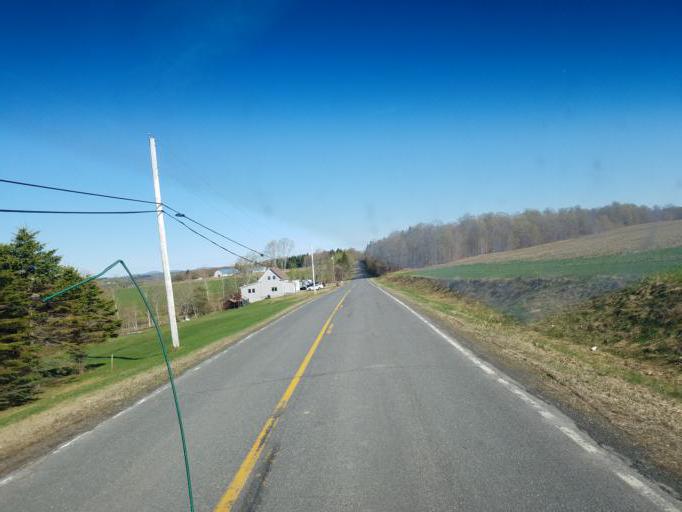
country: US
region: Maine
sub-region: Aroostook County
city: Caribou
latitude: 46.8694
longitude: -68.2105
